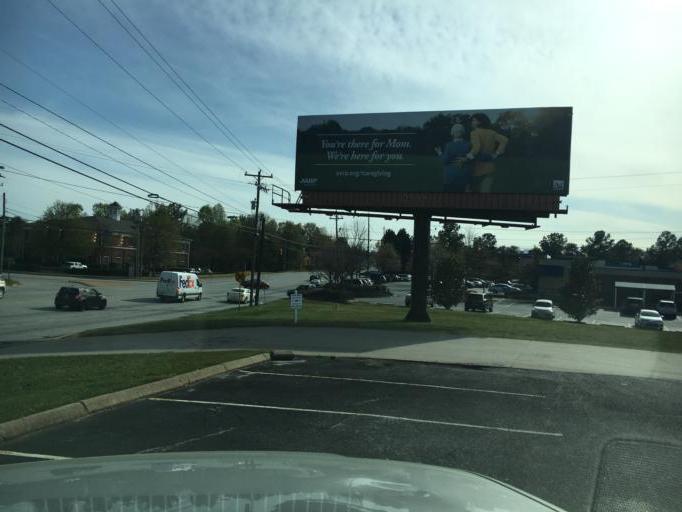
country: US
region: South Carolina
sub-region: Greenville County
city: Greenville
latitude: 34.8364
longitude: -82.3455
